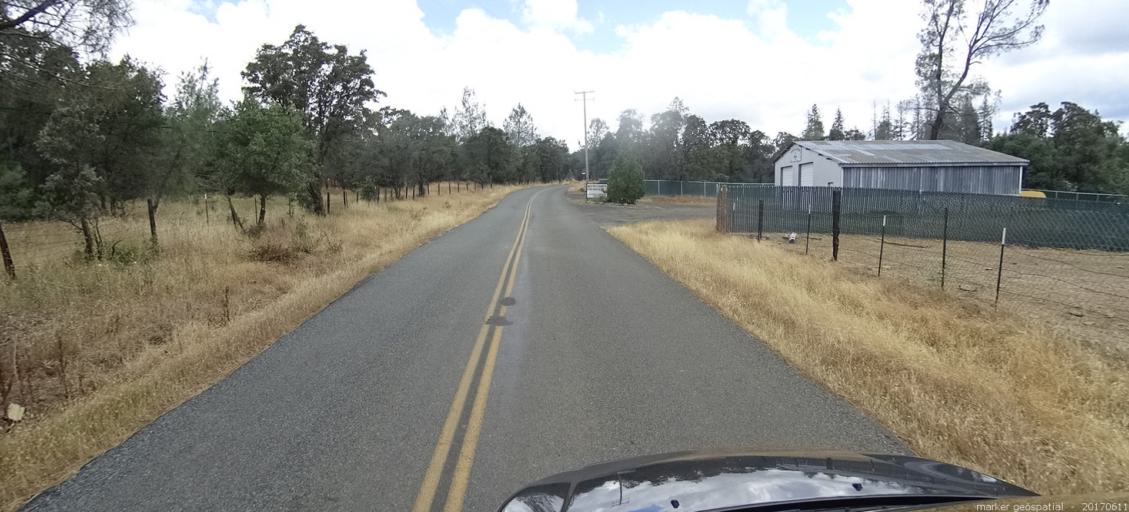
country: US
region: California
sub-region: Butte County
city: Berry Creek
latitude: 39.6415
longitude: -121.5295
